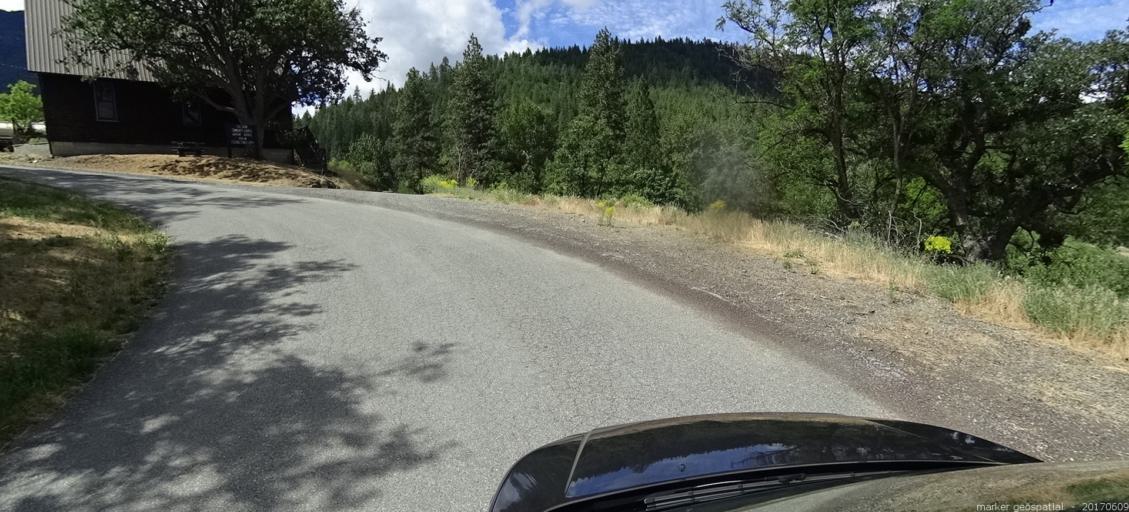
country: US
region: California
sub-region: Siskiyou County
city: Weed
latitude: 41.3088
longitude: -122.8009
